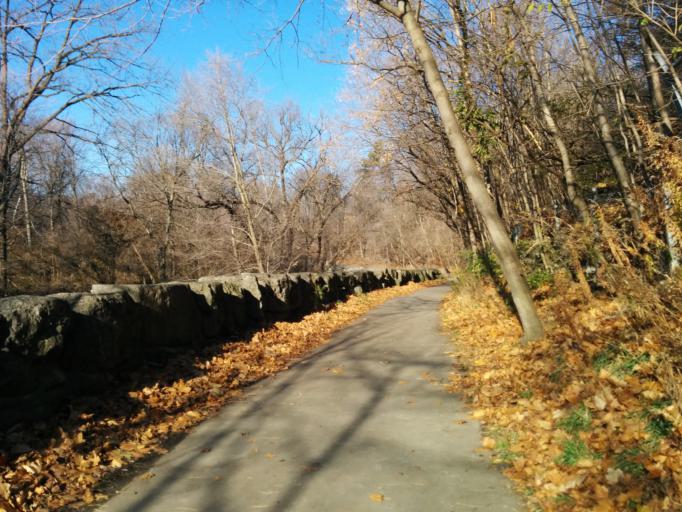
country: CA
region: Ontario
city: Etobicoke
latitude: 43.5936
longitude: -79.5486
